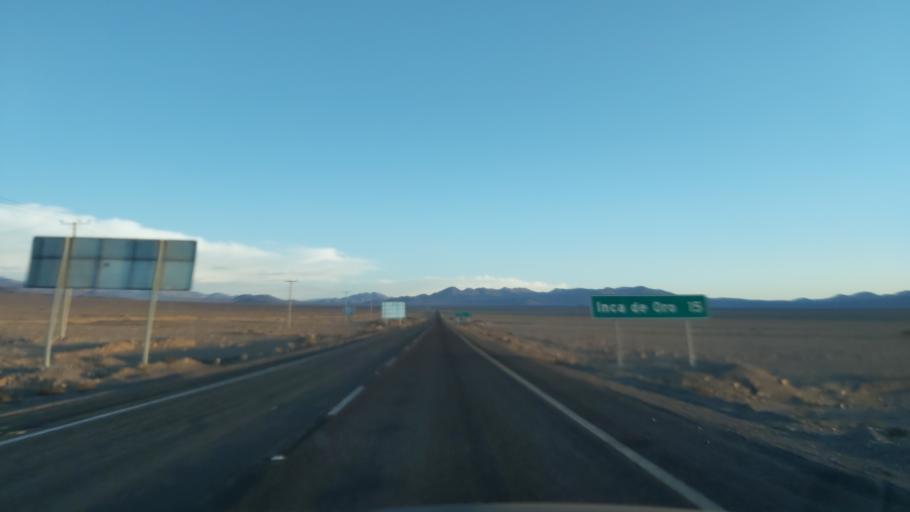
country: CL
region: Atacama
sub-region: Provincia de Chanaral
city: Diego de Almagro
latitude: -26.6305
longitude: -69.9495
